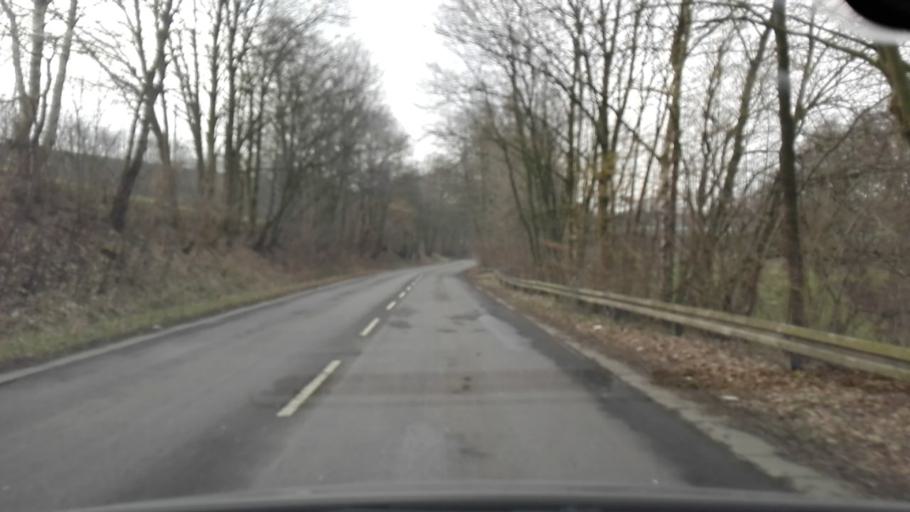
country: DE
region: North Rhine-Westphalia
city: Schwerte
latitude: 51.4660
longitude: 7.5860
